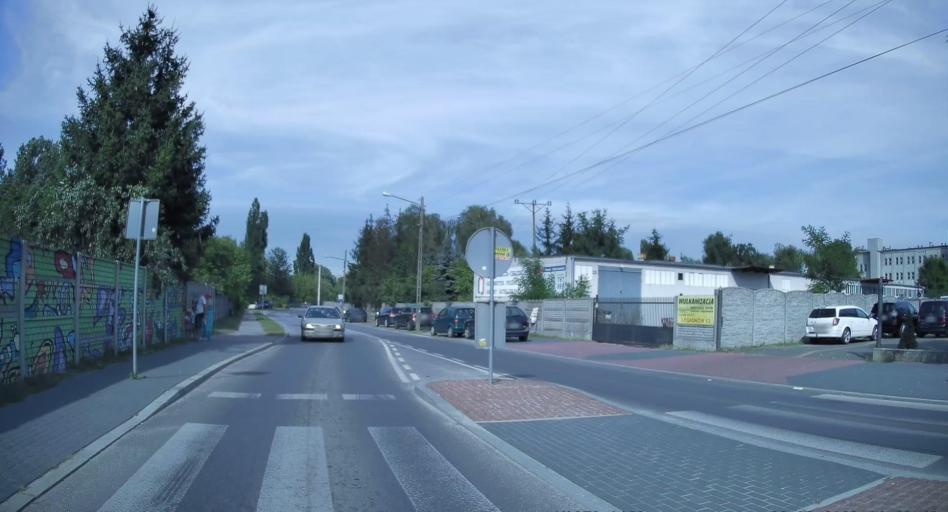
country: PL
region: Lodz Voivodeship
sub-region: Powiat tomaszowski
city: Tomaszow Mazowiecki
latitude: 51.5359
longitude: 19.9969
